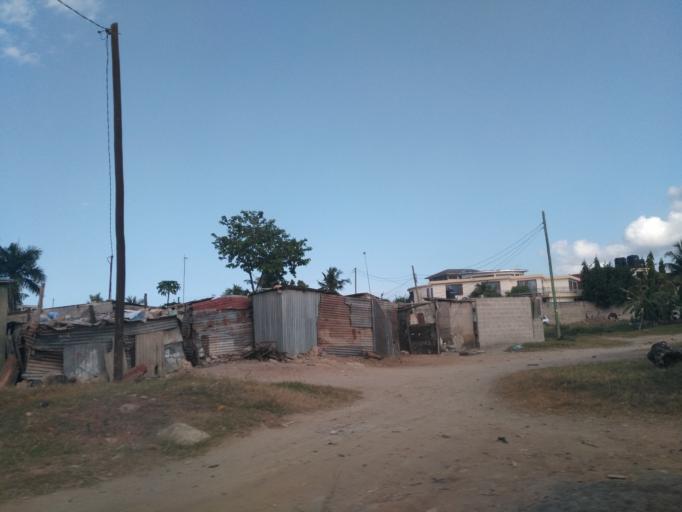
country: TZ
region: Dar es Salaam
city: Magomeni
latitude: -6.7638
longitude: 39.2644
